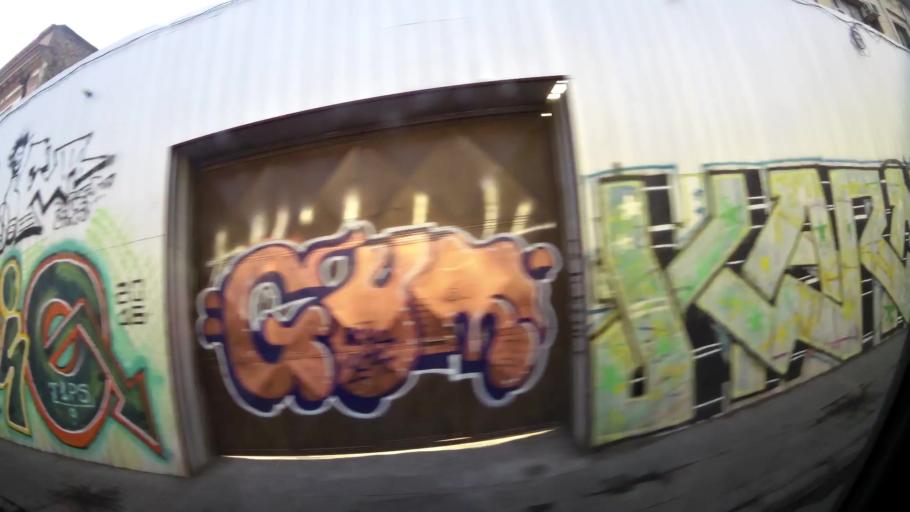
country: CL
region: Santiago Metropolitan
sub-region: Provincia de Santiago
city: Santiago
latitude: -33.4569
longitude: -70.6477
